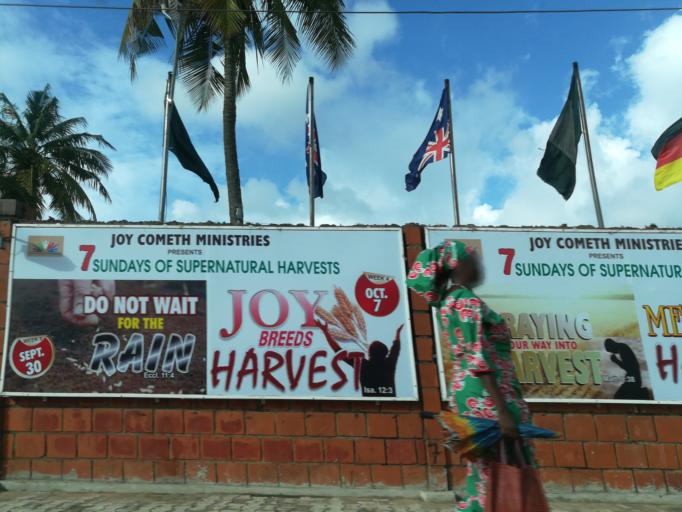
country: NG
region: Lagos
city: Ebute Ikorodu
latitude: 6.5988
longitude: 3.4958
